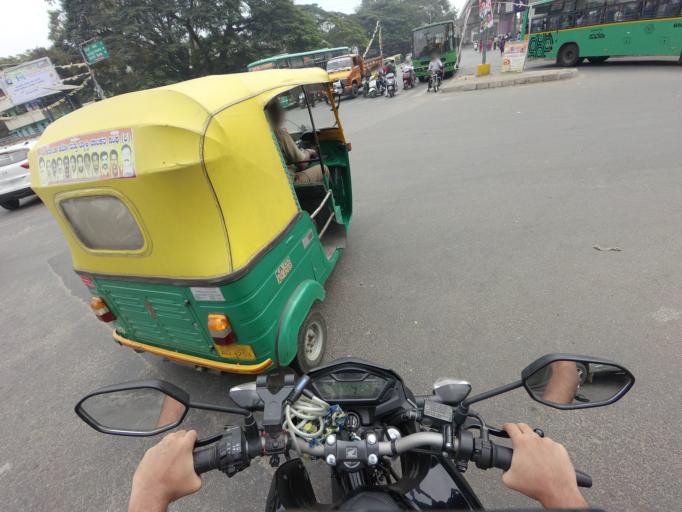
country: IN
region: Karnataka
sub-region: Bangalore Urban
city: Bangalore
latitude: 12.9749
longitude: 77.5483
